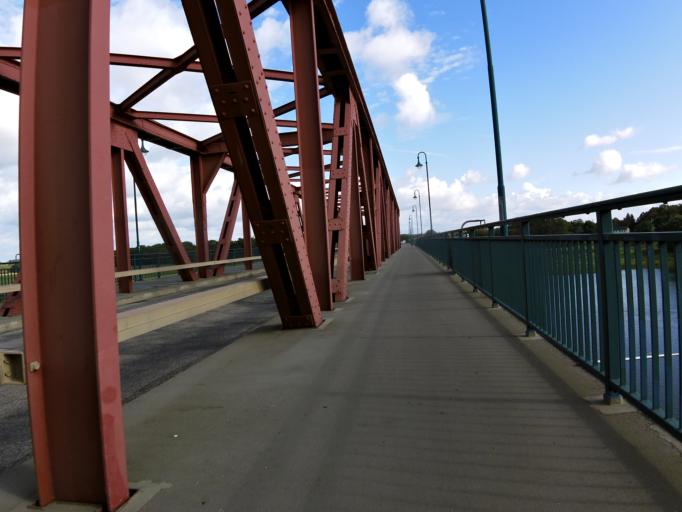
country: DE
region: Saxony-Anhalt
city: Schonebeck
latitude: 52.0241
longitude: 11.7385
